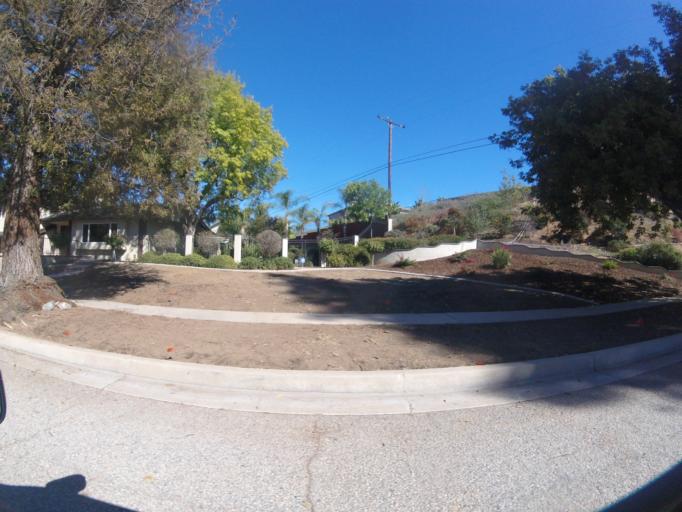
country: US
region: California
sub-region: San Bernardino County
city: Mentone
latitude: 34.0279
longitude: -117.1392
